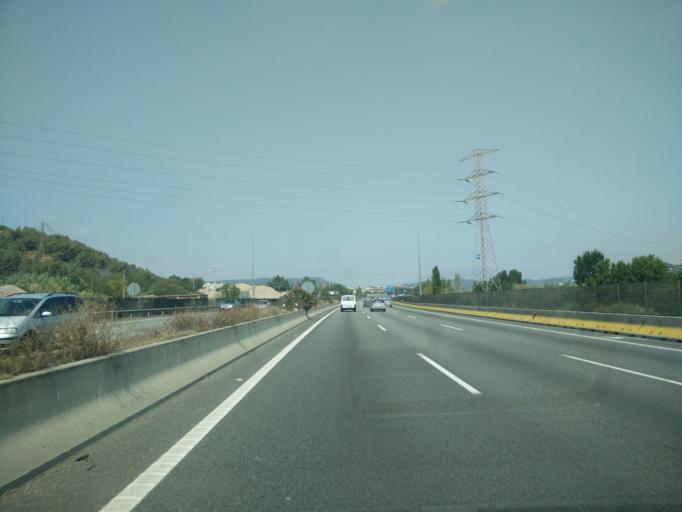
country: ES
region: Catalonia
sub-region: Provincia de Barcelona
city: Sant Andreu de la Barca
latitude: 41.4402
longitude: 1.9881
